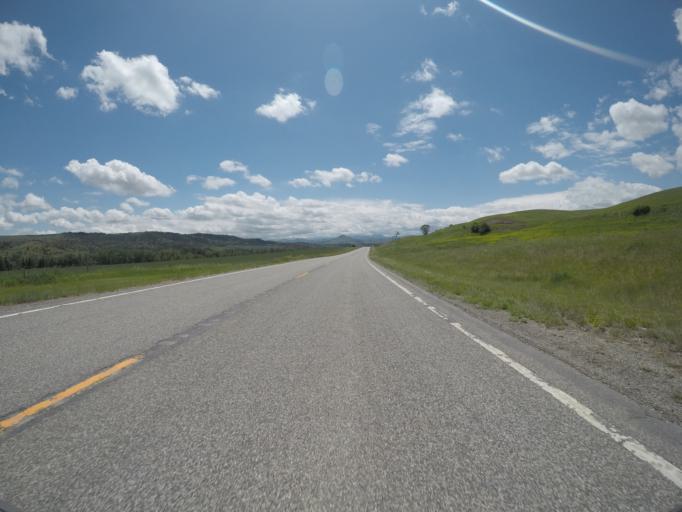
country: US
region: Montana
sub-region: Sweet Grass County
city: Big Timber
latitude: 45.7626
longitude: -109.9900
